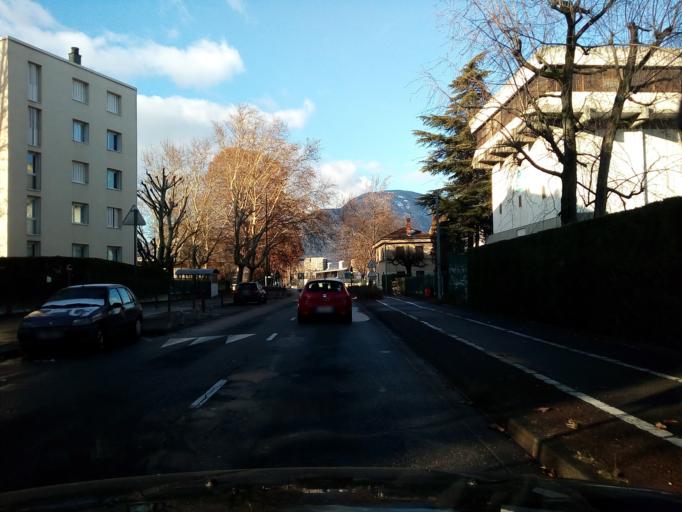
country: FR
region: Rhone-Alpes
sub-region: Departement de l'Isere
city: Saint-Martin-d'Heres
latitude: 45.1737
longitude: 5.7456
